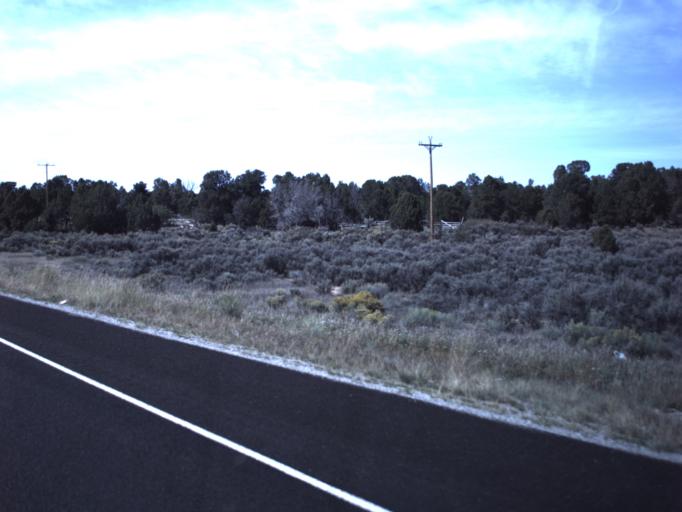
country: US
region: Colorado
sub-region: Dolores County
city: Dove Creek
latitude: 37.8379
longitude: -109.1163
